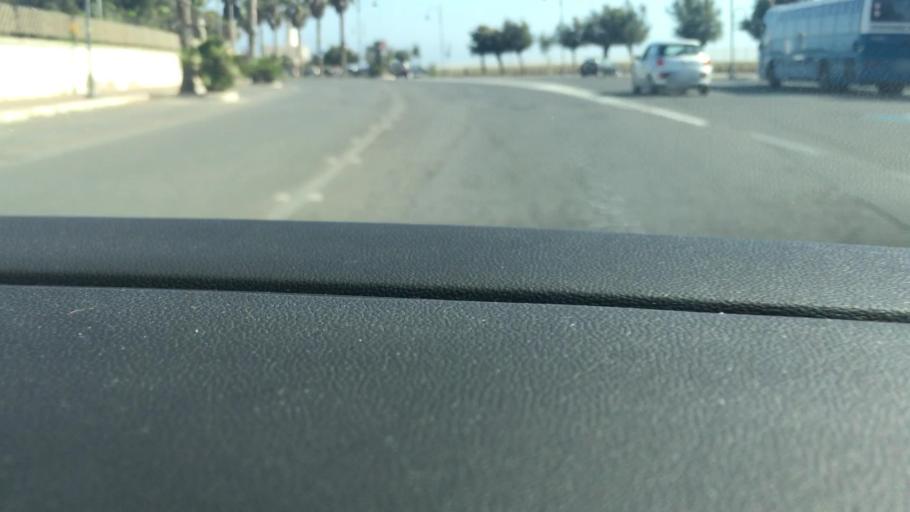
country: IT
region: Latium
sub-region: Citta metropolitana di Roma Capitale
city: Anzio
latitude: 41.4484
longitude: 12.6196
